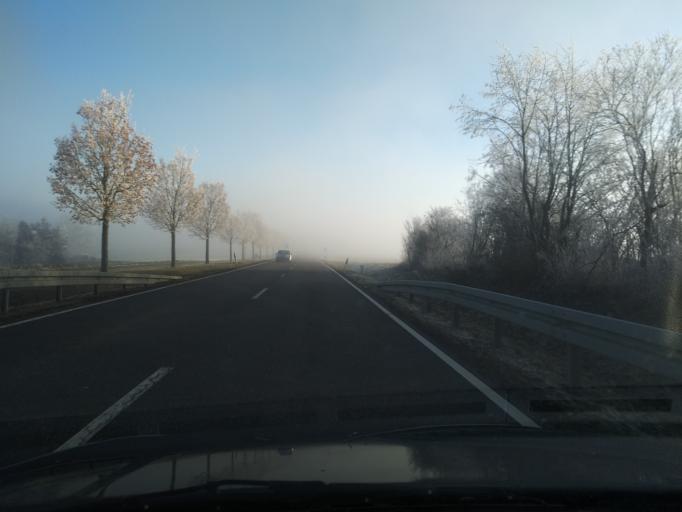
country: DE
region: Baden-Wuerttemberg
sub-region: Regierungsbezirk Stuttgart
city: Deckenpfronn
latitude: 48.6397
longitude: 8.8247
